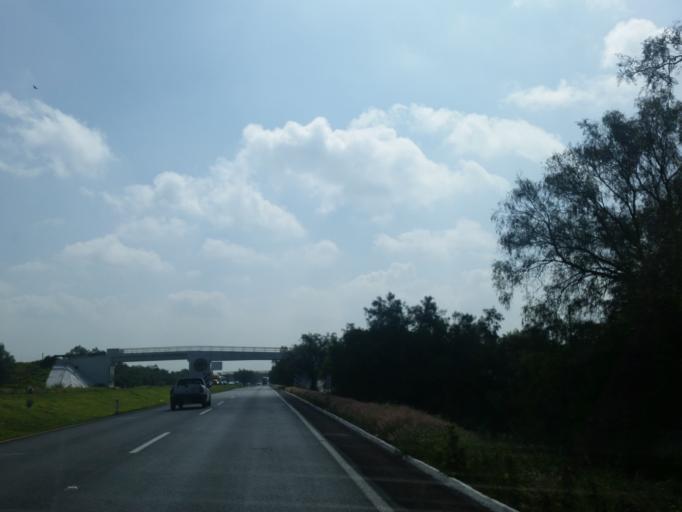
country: MX
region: Mexico
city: Acolman
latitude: 19.6227
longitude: -98.9385
